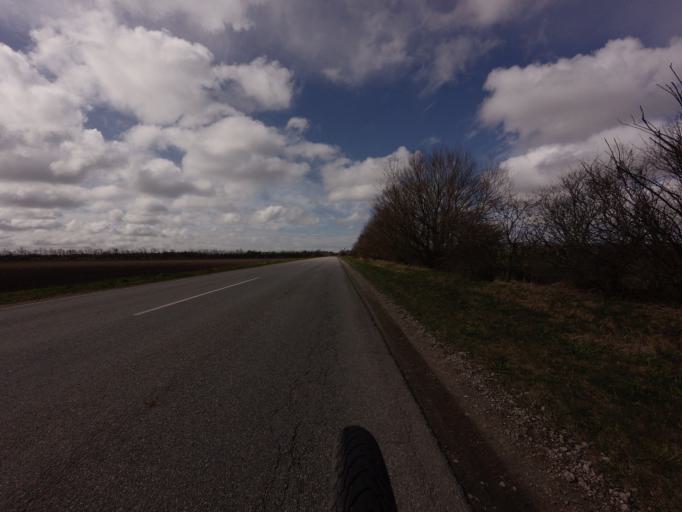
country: DK
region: North Denmark
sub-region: Hjorring Kommune
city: Vra
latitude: 57.3589
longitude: 9.8679
